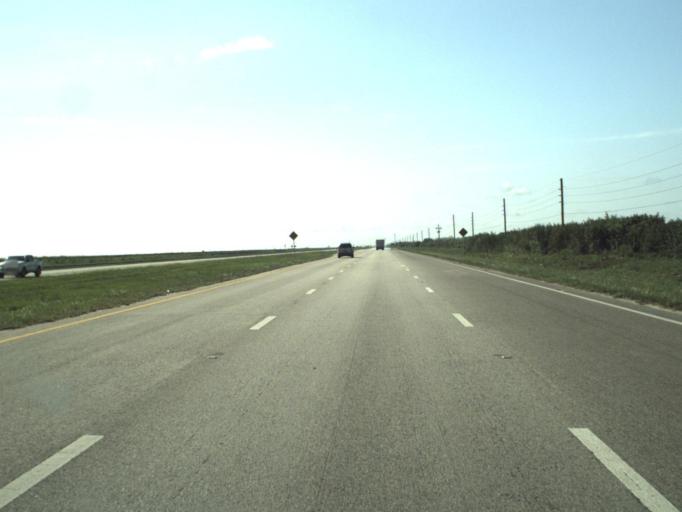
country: US
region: Florida
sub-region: Palm Beach County
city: Belle Glade Camp
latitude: 26.4312
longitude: -80.6125
